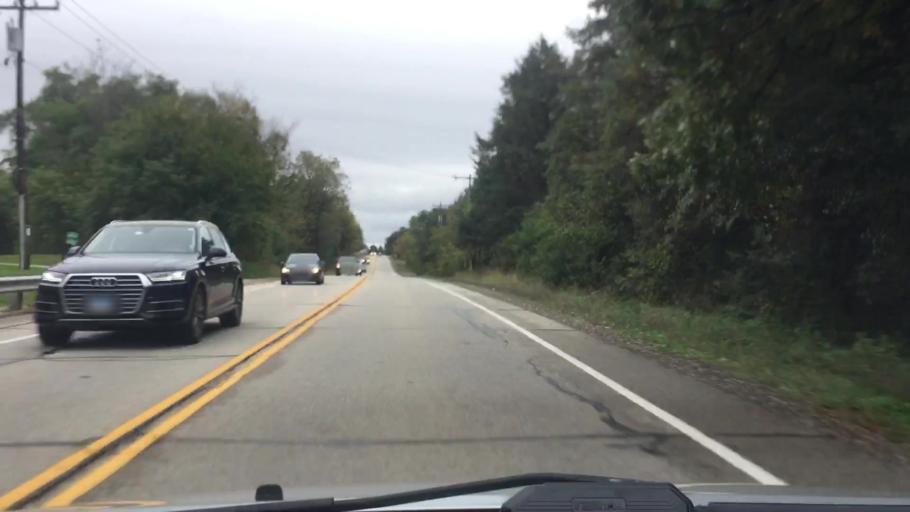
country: US
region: Wisconsin
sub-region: Jefferson County
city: Palmyra
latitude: 42.7851
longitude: -88.5600
